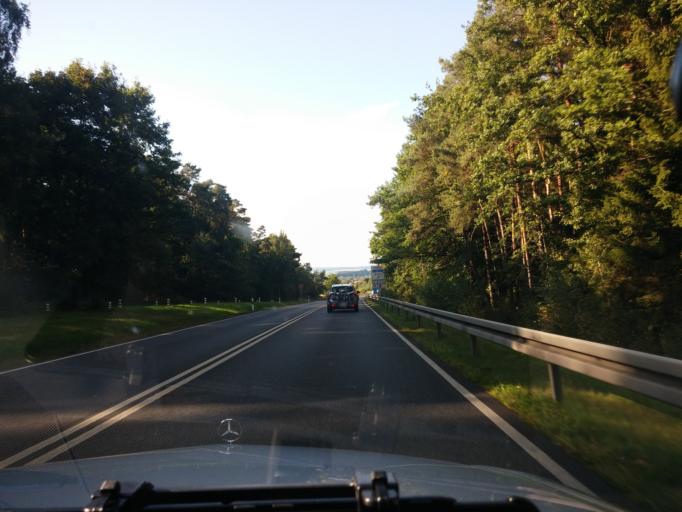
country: DE
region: Hesse
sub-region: Regierungsbezirk Kassel
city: Eichenzell
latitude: 50.4805
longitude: 9.6909
